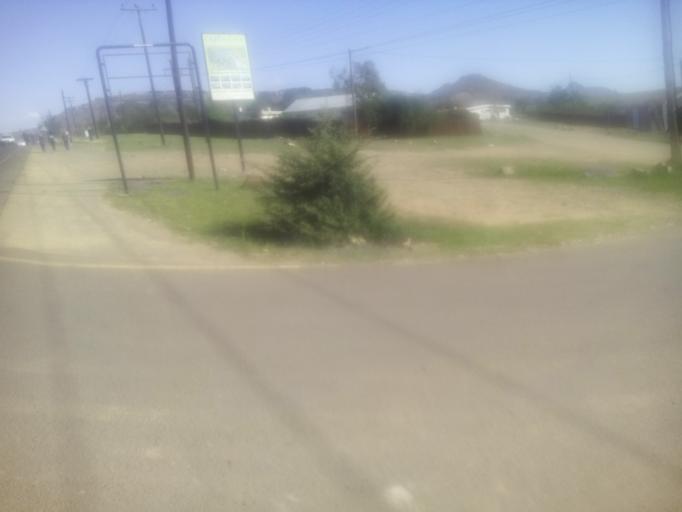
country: LS
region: Maseru
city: Maseru
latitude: -29.3094
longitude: 27.4659
